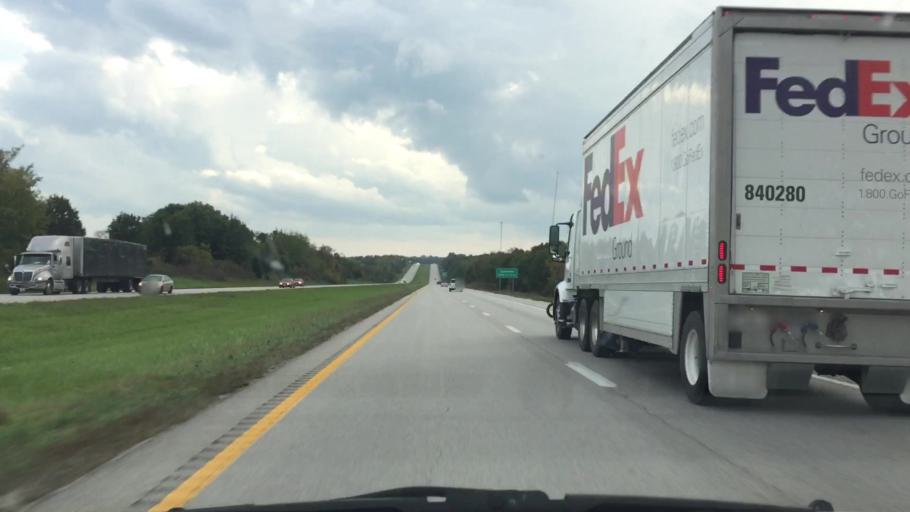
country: US
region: Missouri
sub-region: Clinton County
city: Cameron
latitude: 39.7779
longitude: -94.2104
